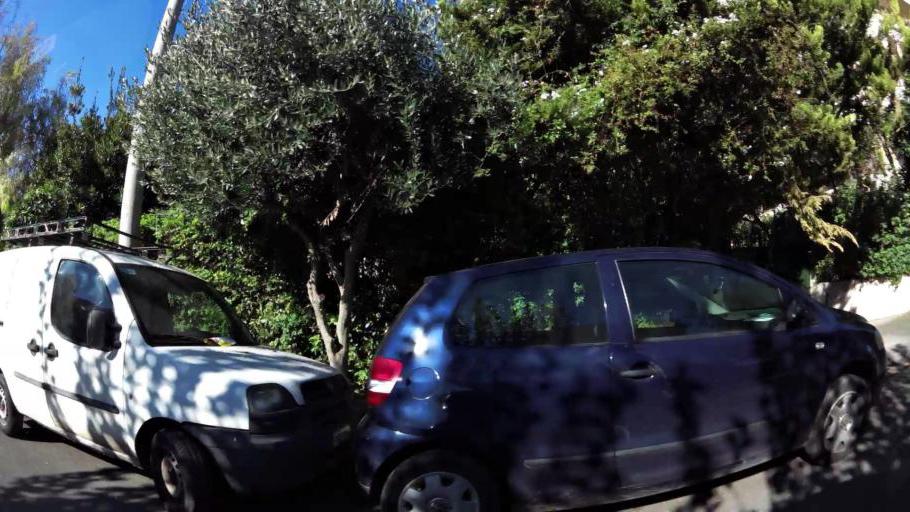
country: GR
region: Attica
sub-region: Nomarchia Athinas
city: Khalandrion
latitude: 38.0225
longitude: 23.8087
